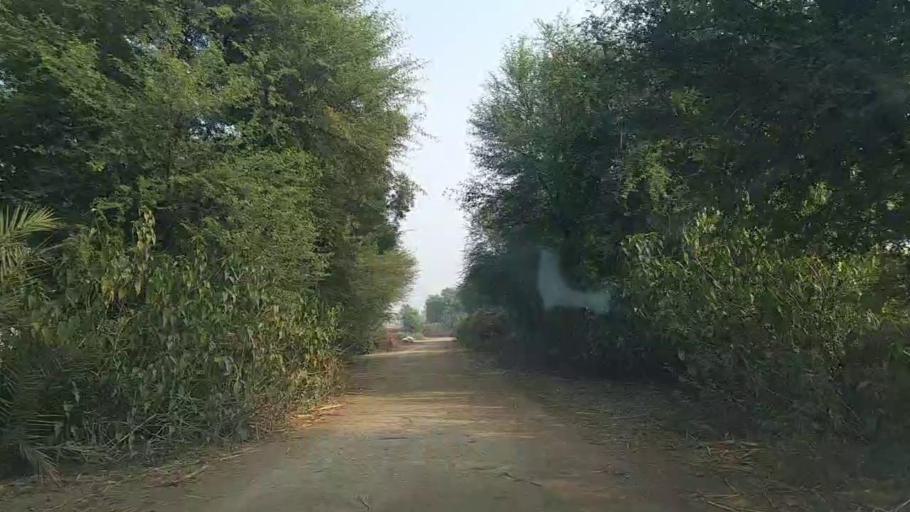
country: PK
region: Sindh
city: Sanghar
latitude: 26.0709
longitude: 68.8823
